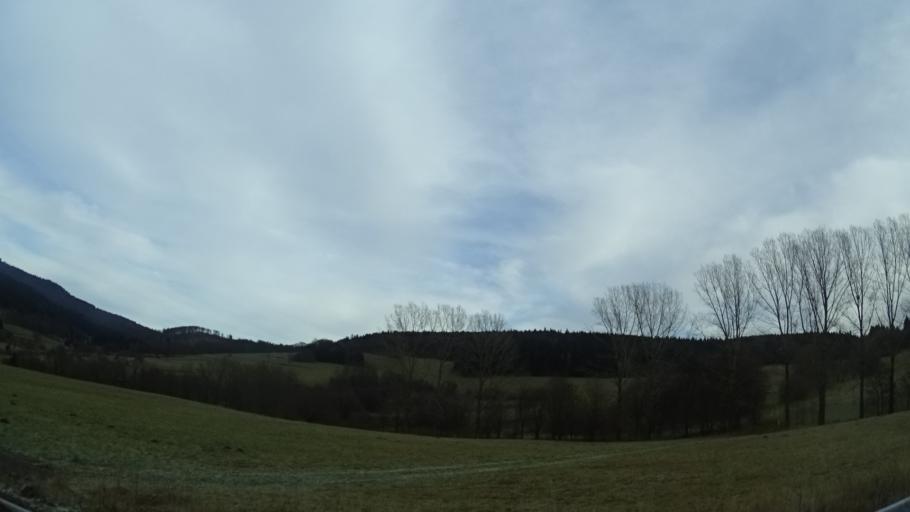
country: DE
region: Thuringia
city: Brotterode
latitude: 50.8216
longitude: 10.4560
